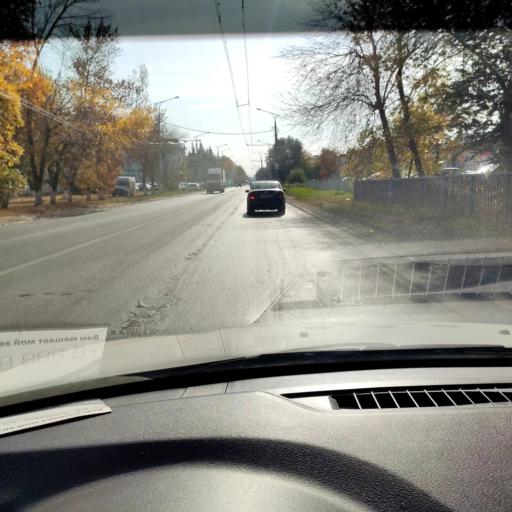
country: RU
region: Samara
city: Tol'yatti
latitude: 53.5432
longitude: 49.4446
